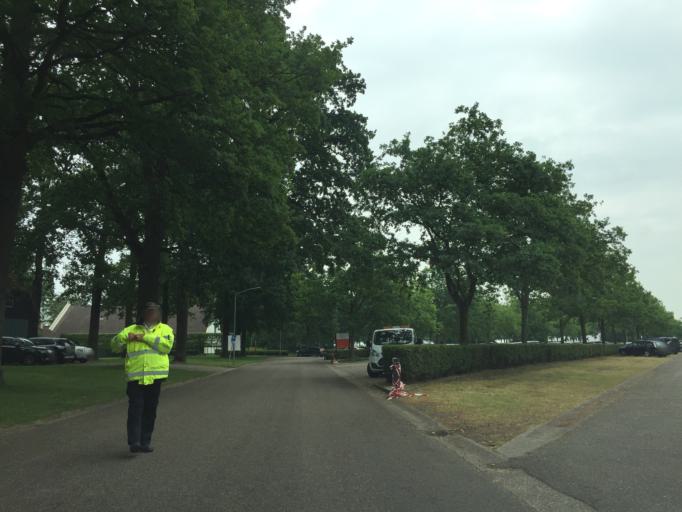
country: NL
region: North Brabant
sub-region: Gemeente Maasdonk
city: Geffen
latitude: 51.7131
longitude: 5.4135
